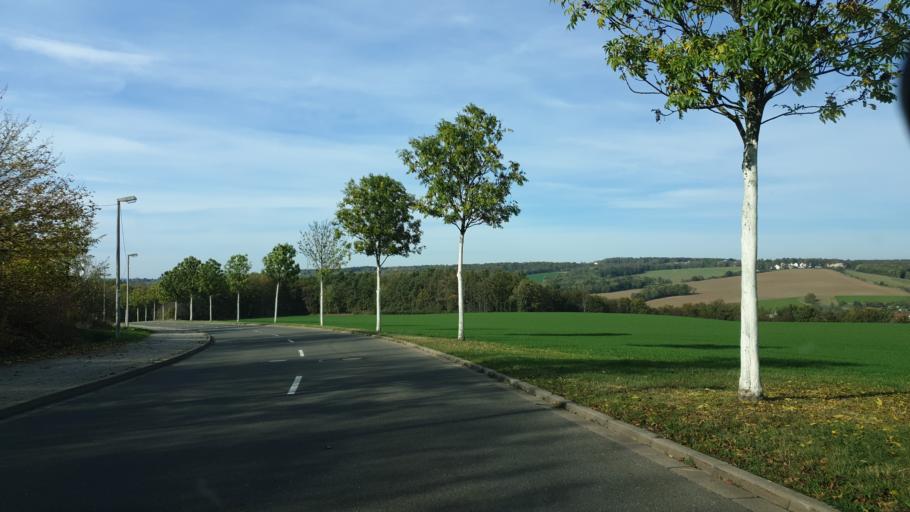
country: DE
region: Thuringia
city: Schwaara
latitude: 50.9054
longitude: 12.1098
